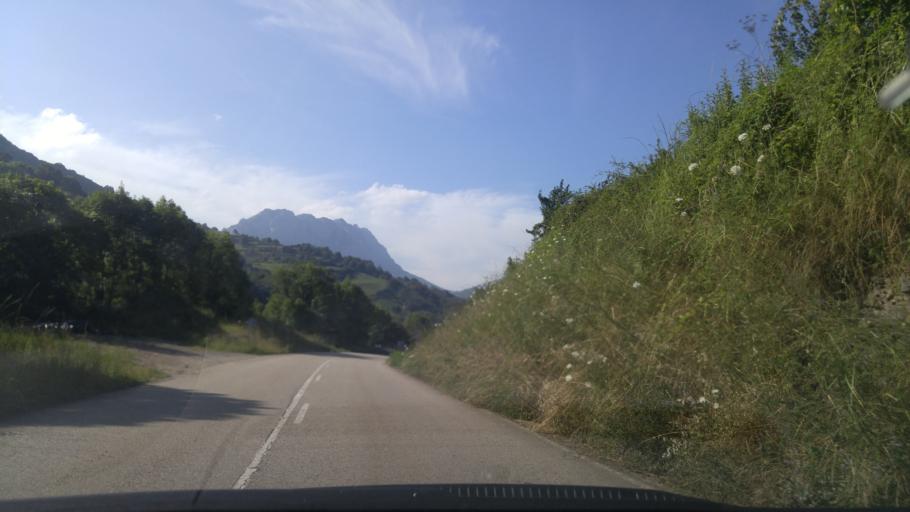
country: ES
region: Asturias
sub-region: Province of Asturias
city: Barzana
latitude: 43.1784
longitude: -5.9935
